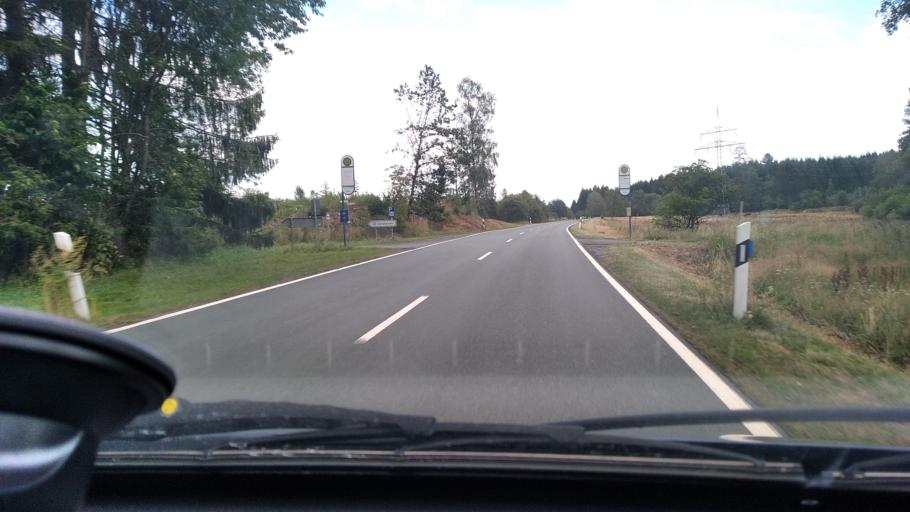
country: DE
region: Hesse
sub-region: Regierungsbezirk Giessen
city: Siegbach
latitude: 50.7893
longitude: 8.3670
